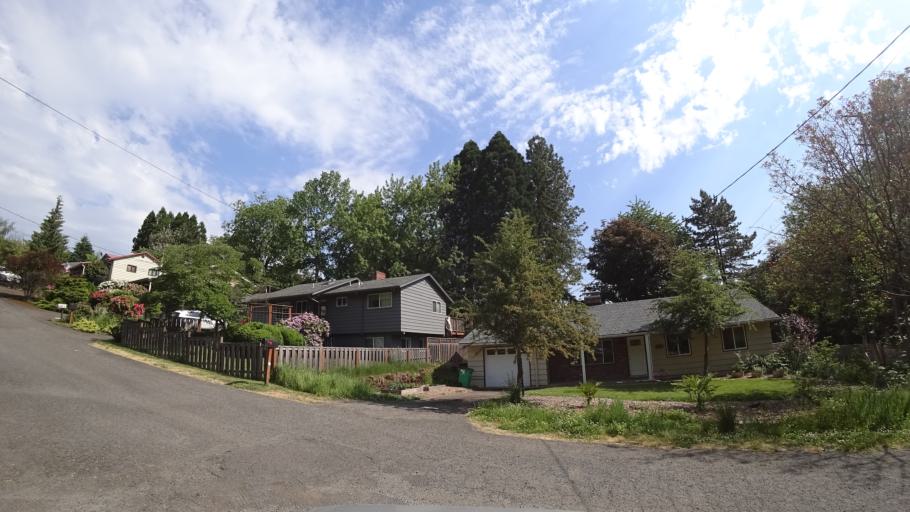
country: US
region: Oregon
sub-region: Washington County
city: Metzger
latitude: 45.4520
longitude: -122.7434
